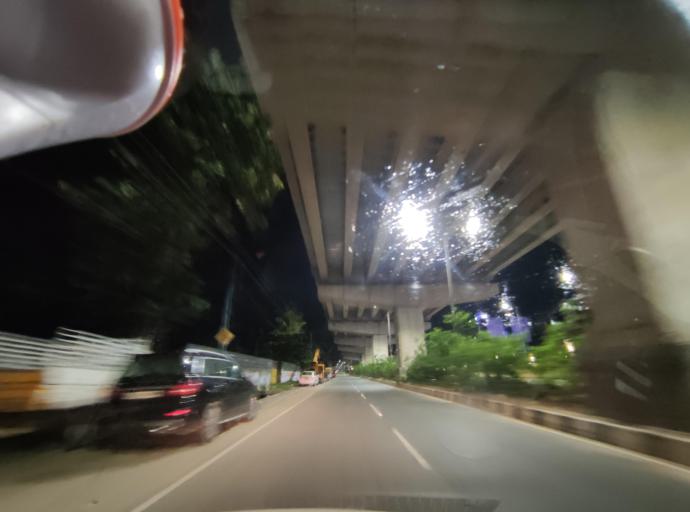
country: IN
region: Kerala
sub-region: Thiruvananthapuram
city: Thiruvananthapuram
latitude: 8.4879
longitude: 76.9268
